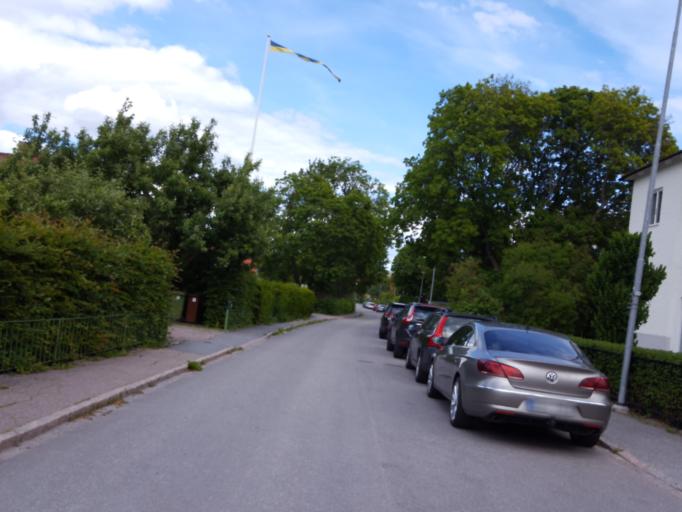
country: SE
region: Uppsala
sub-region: Uppsala Kommun
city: Uppsala
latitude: 59.8443
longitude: 17.6288
